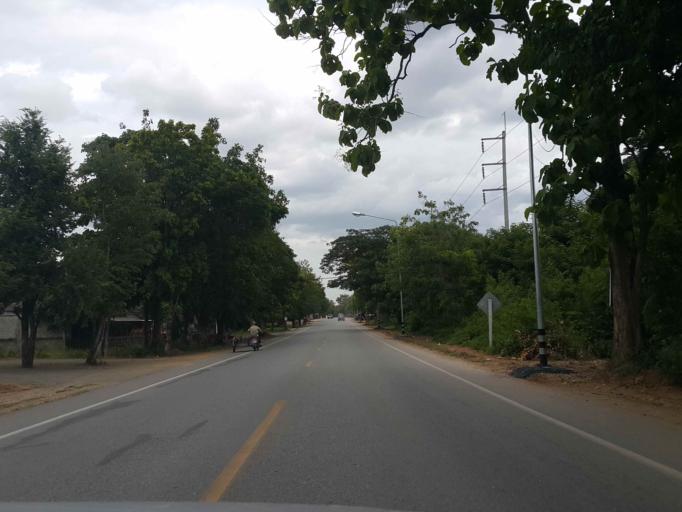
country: TH
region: Lamphun
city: Pa Sang
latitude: 18.4444
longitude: 98.8819
